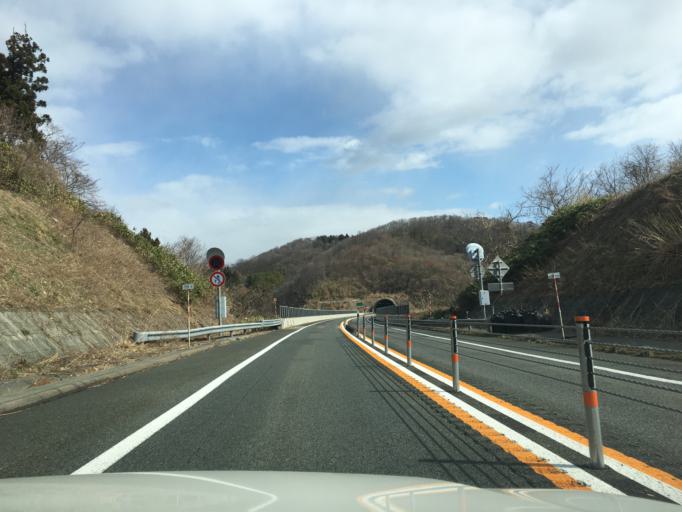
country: JP
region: Akita
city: Akita Shi
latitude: 39.5288
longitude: 140.0624
